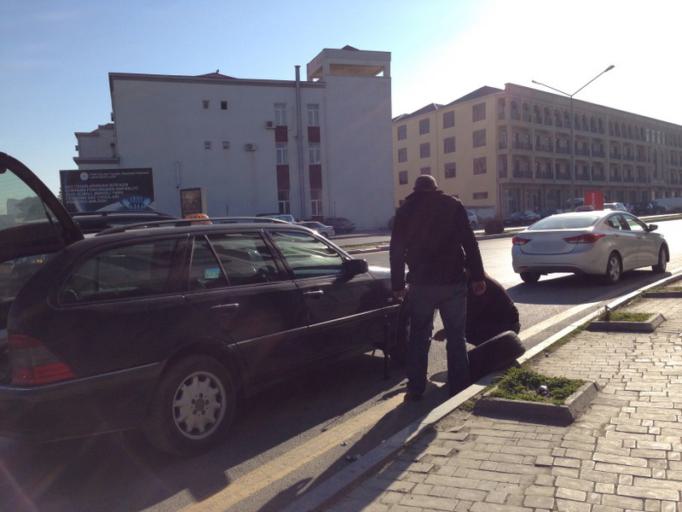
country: AZ
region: Baki
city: Baku
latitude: 40.4086
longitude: 49.8639
